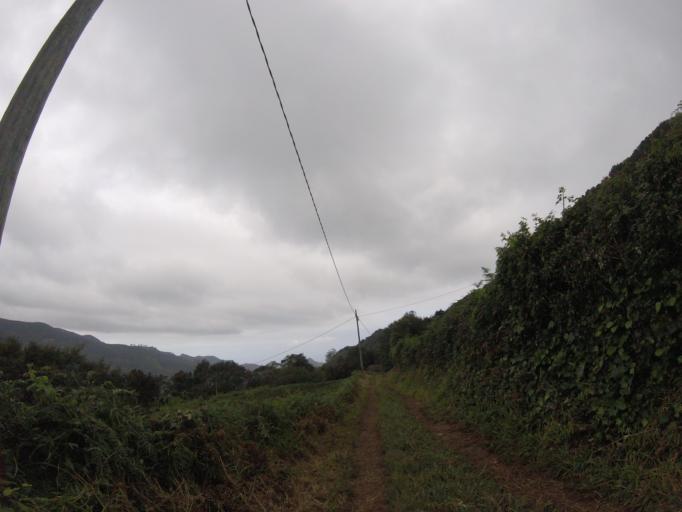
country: ES
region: Canary Islands
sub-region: Provincia de Santa Cruz de Tenerife
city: Tegueste
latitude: 28.5412
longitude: -16.2779
